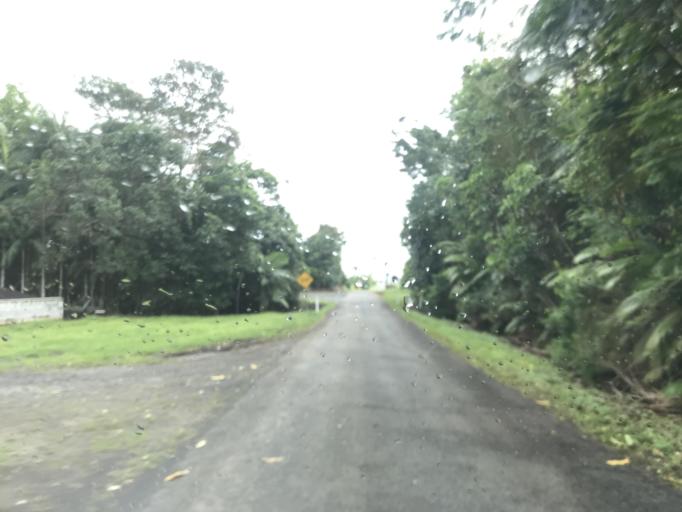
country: AU
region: Queensland
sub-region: Cassowary Coast
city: Innisfail
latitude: -17.4854
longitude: 145.9890
